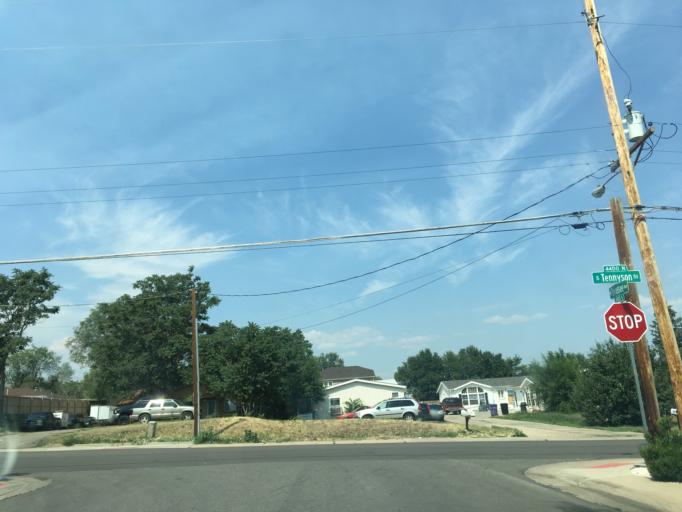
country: US
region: Colorado
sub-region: Jefferson County
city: Lakewood
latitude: 39.6987
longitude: -105.0435
